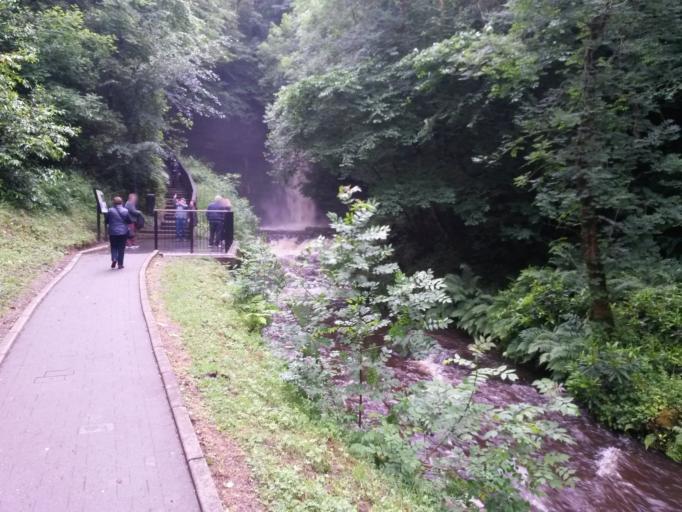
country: IE
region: Connaught
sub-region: Sligo
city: Sligo
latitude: 54.3402
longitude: -8.3683
